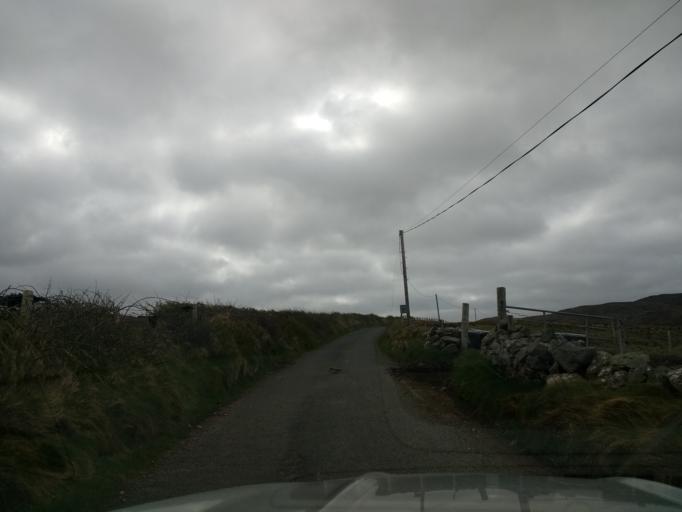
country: IE
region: Ulster
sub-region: County Donegal
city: Ramelton
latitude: 55.2694
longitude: -7.6477
